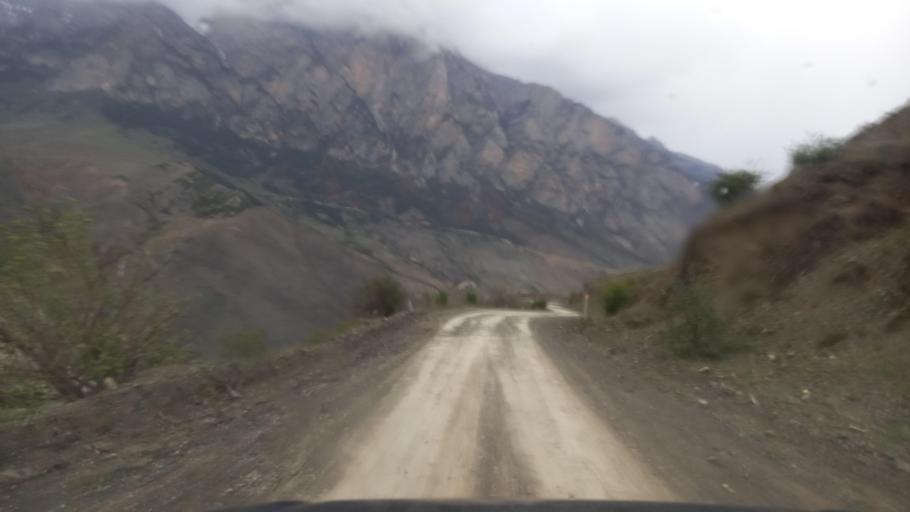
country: RU
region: North Ossetia
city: Mizur
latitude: 42.8580
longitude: 44.1588
